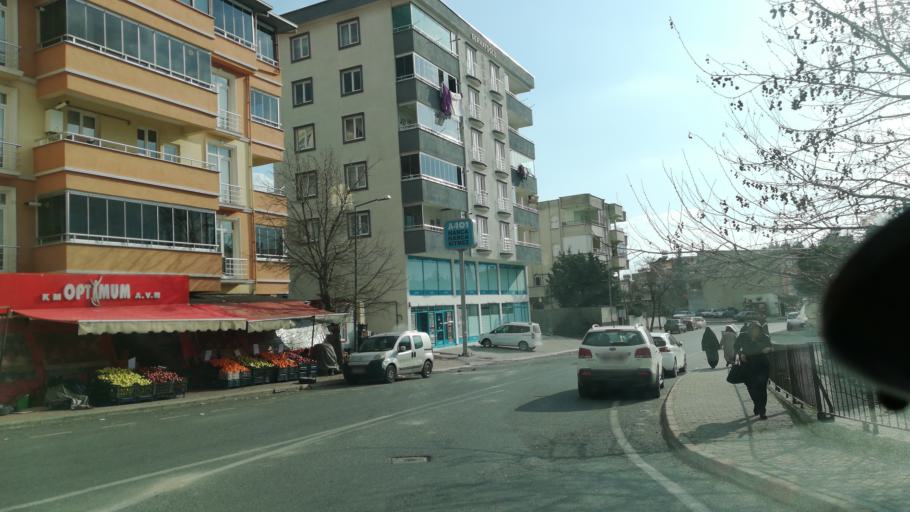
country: TR
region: Kahramanmaras
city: Kahramanmaras
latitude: 37.5877
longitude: 36.9377
